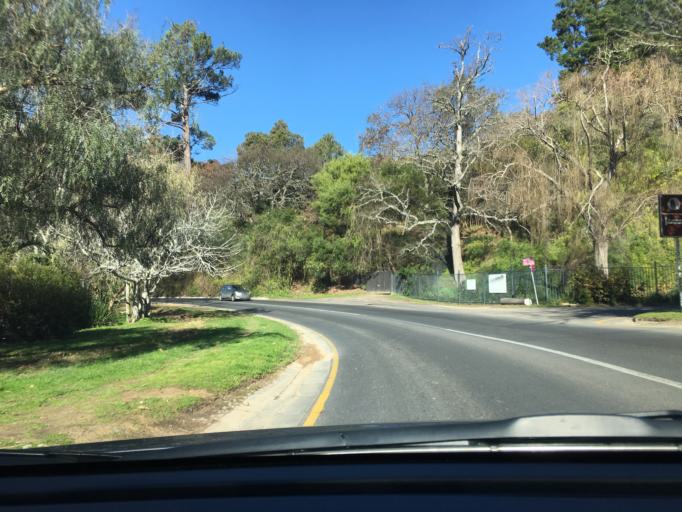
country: ZA
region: Western Cape
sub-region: City of Cape Town
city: Constantia
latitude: -34.0148
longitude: 18.4152
